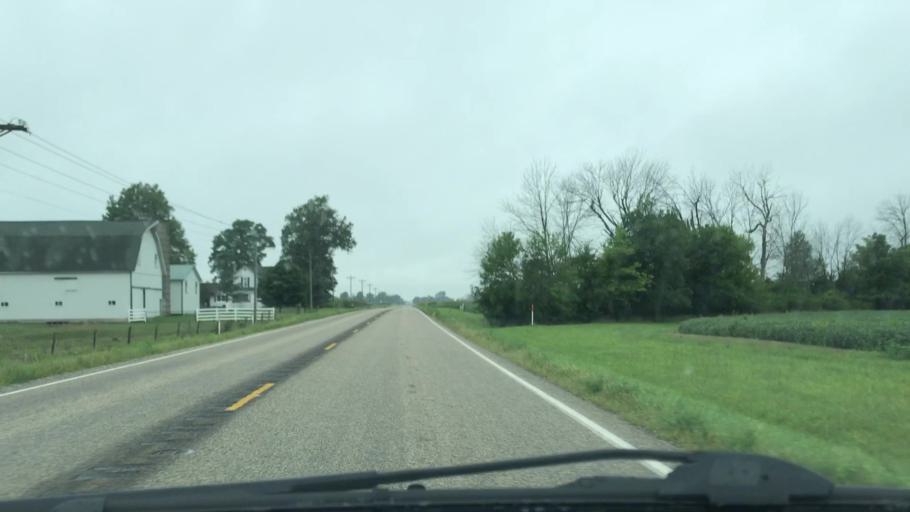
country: US
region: Indiana
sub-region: Boone County
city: Dale
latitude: 40.1272
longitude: -86.3570
